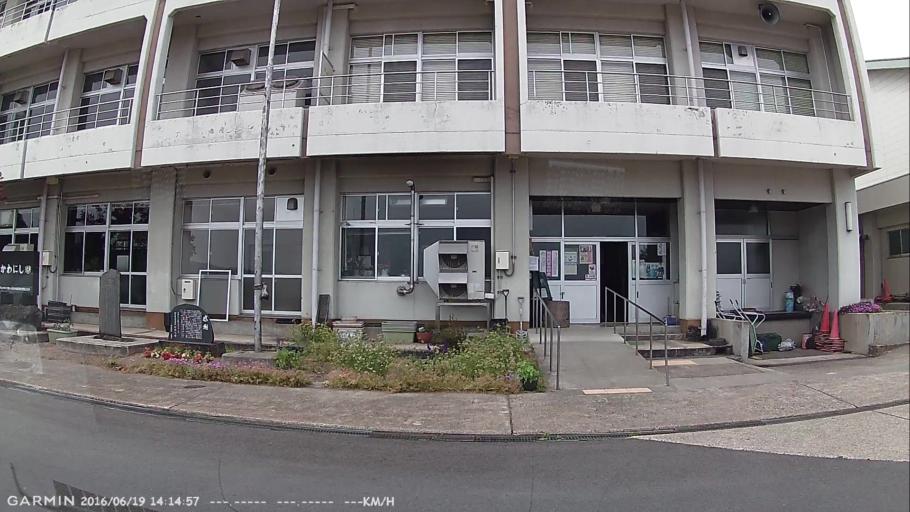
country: JP
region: Fukushima
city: Kitakata
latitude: 37.5877
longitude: 139.8111
